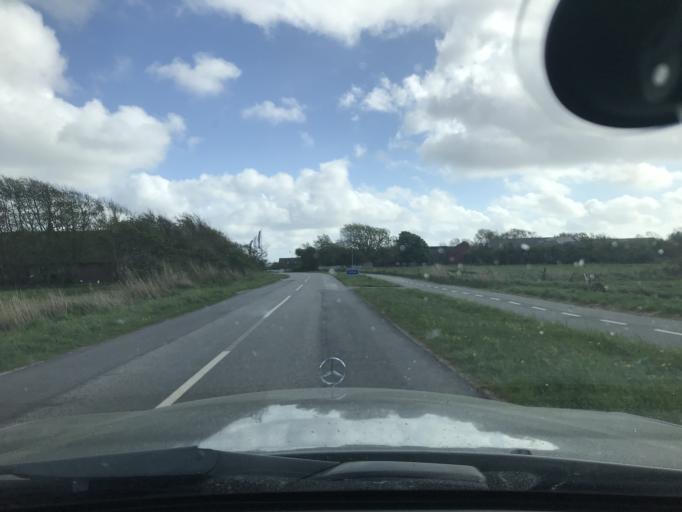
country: DE
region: Schleswig-Holstein
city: List
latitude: 55.1673
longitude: 8.5548
